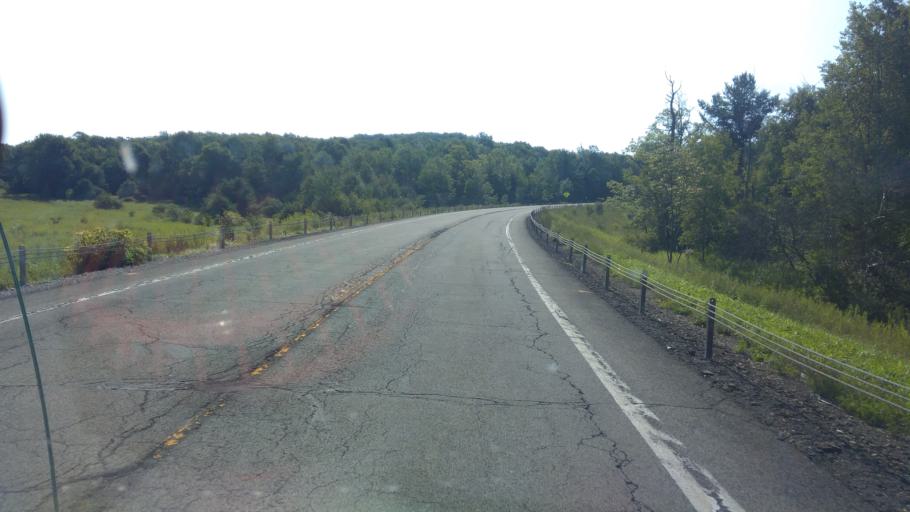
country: US
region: New York
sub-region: Allegany County
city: Cuba
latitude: 42.1728
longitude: -78.2472
